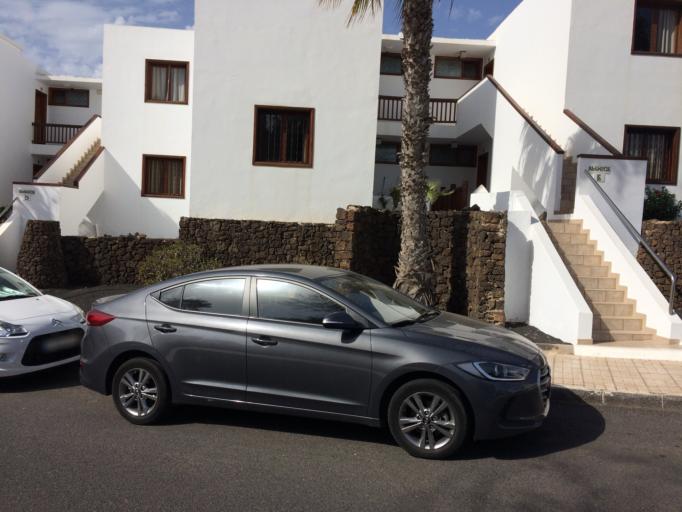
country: ES
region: Canary Islands
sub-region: Provincia de Las Palmas
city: Arrecife
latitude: 28.9950
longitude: -13.4956
